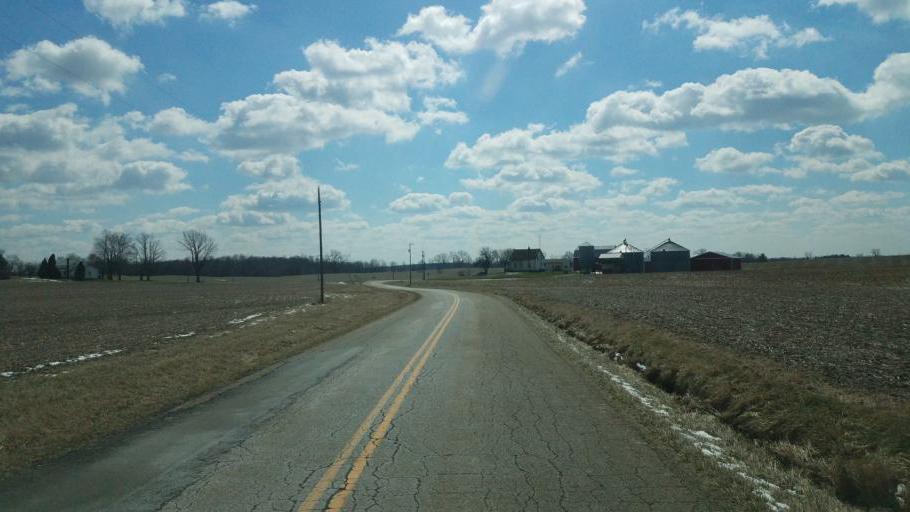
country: US
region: Ohio
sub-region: Knox County
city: Mount Vernon
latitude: 40.3293
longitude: -82.5424
